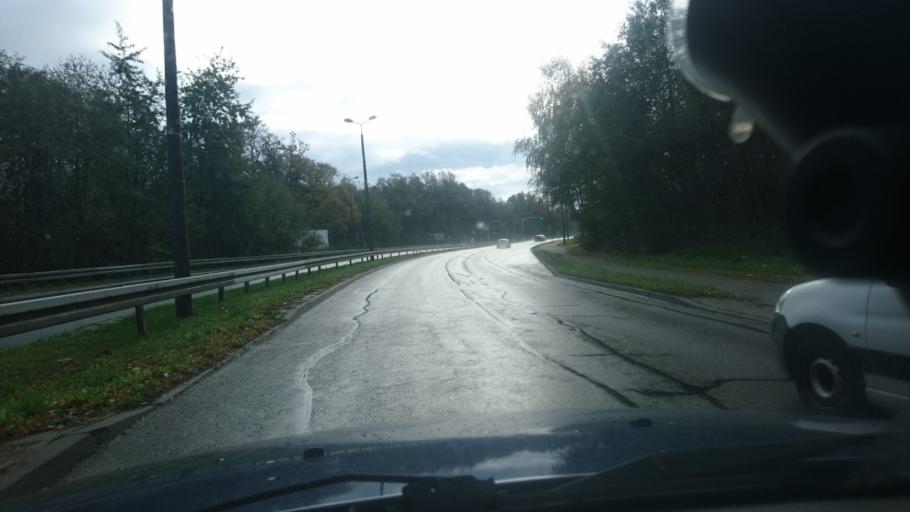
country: PL
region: Silesian Voivodeship
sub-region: Powiat bielski
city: Mazancowice
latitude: 49.8373
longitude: 19.0080
